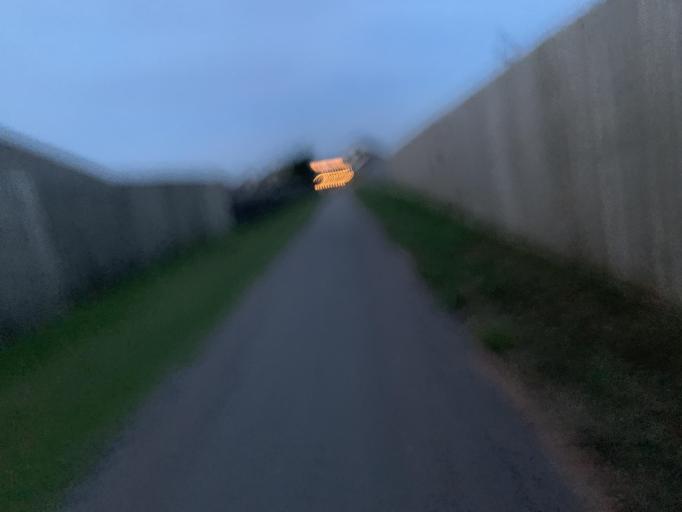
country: US
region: Oklahoma
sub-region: Oklahoma County
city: Edmond
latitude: 35.6620
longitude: -97.5744
